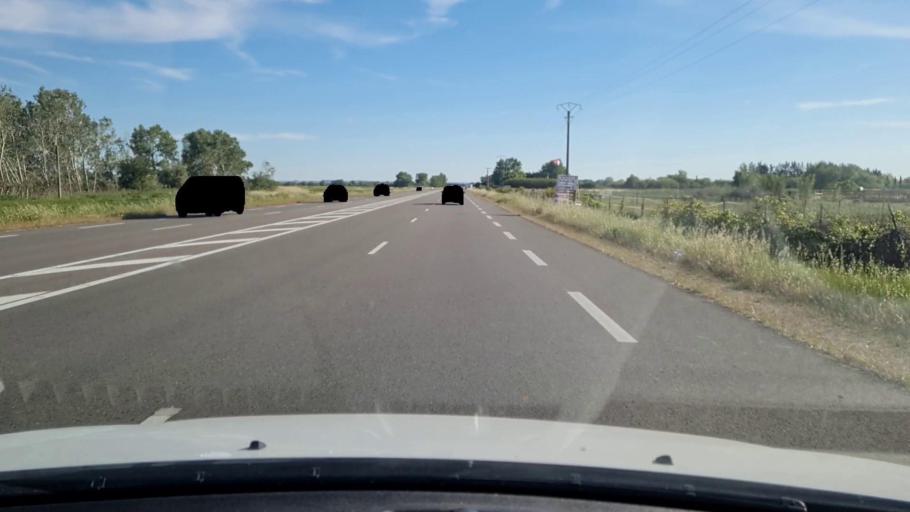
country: FR
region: Languedoc-Roussillon
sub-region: Departement de l'Herault
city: Marsillargues
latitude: 43.6446
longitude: 4.1965
